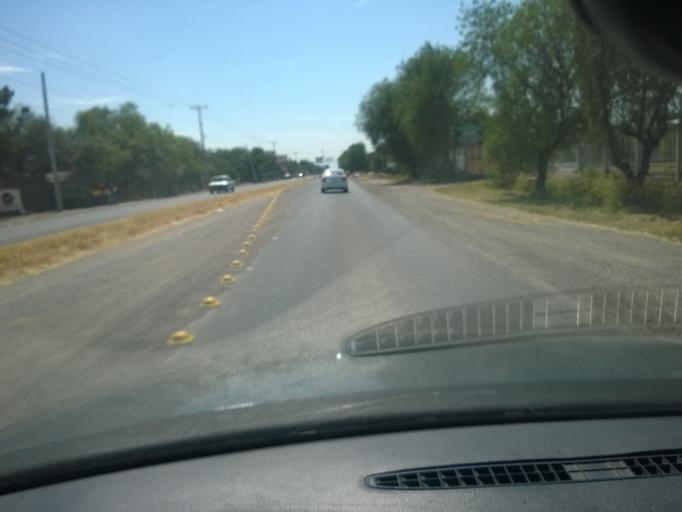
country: MX
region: Guanajuato
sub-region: Leon
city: El CERESO
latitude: 20.9913
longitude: -101.7026
